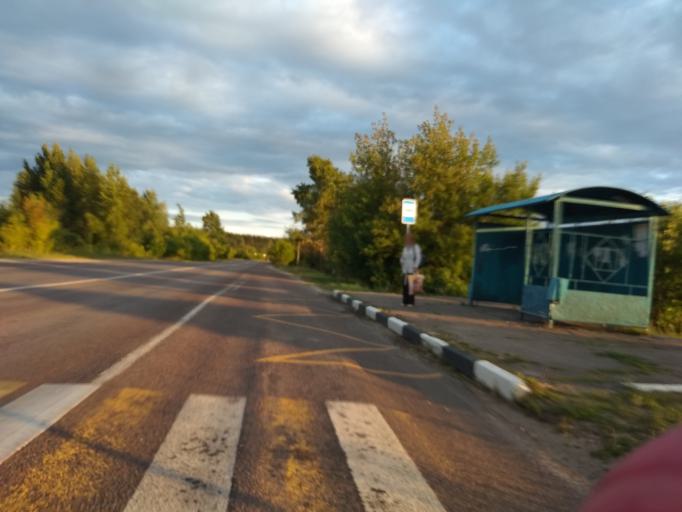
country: RU
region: Moskovskaya
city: Kerva
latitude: 55.5902
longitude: 39.7009
